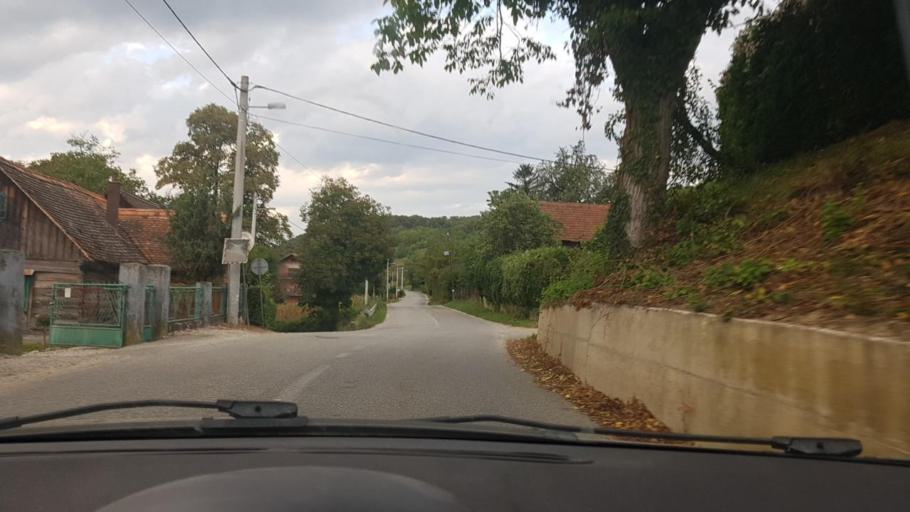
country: HR
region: Grad Zagreb
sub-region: Sesvete
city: Sesvete
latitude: 45.9115
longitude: 16.1674
